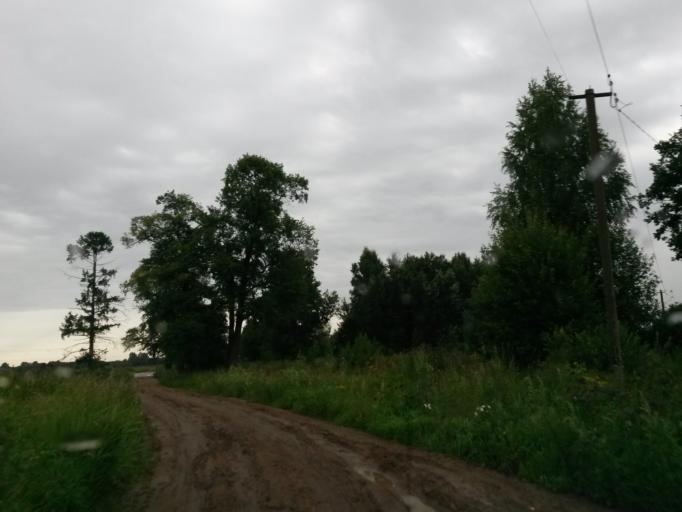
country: RU
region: Jaroslavl
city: Tutayev
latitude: 57.9484
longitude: 39.4455
